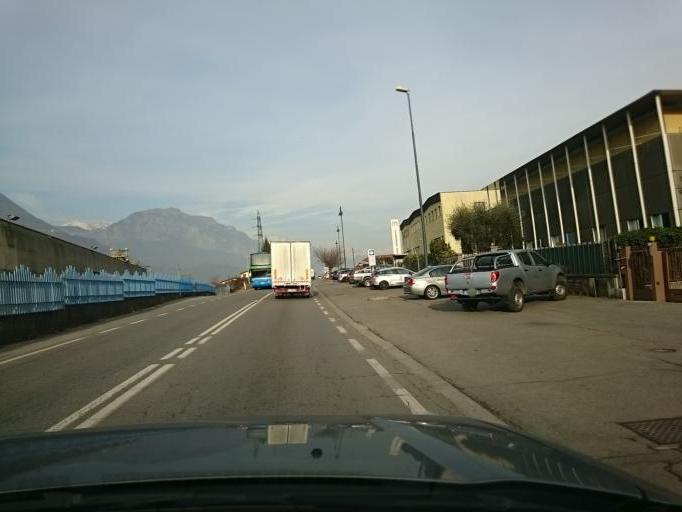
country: IT
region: Lombardy
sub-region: Provincia di Brescia
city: Gratacasolo
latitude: 45.8334
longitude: 10.1321
